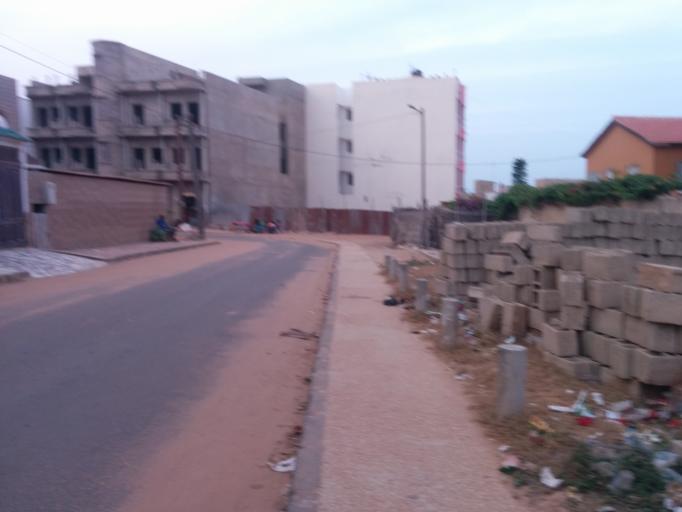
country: SN
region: Dakar
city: Grand Dakar
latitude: 14.7615
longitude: -17.4548
